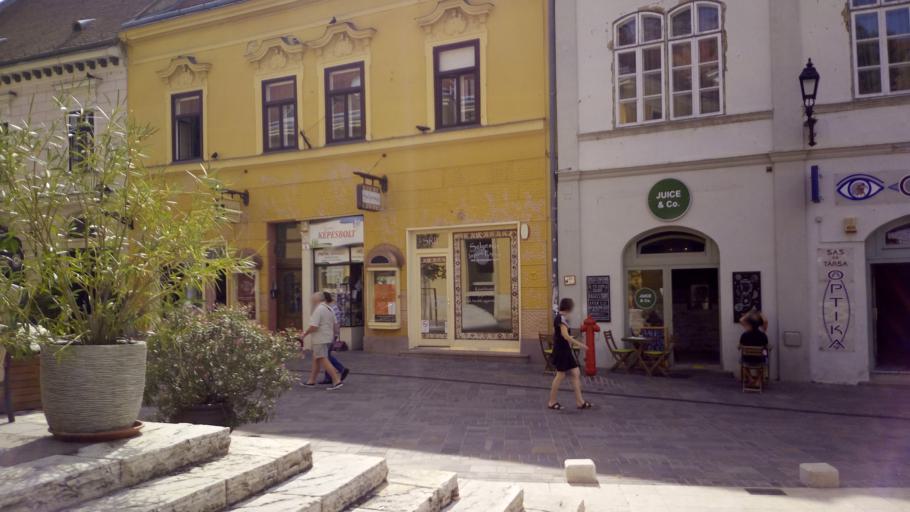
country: HU
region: Baranya
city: Pecs
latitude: 46.0755
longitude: 18.2273
